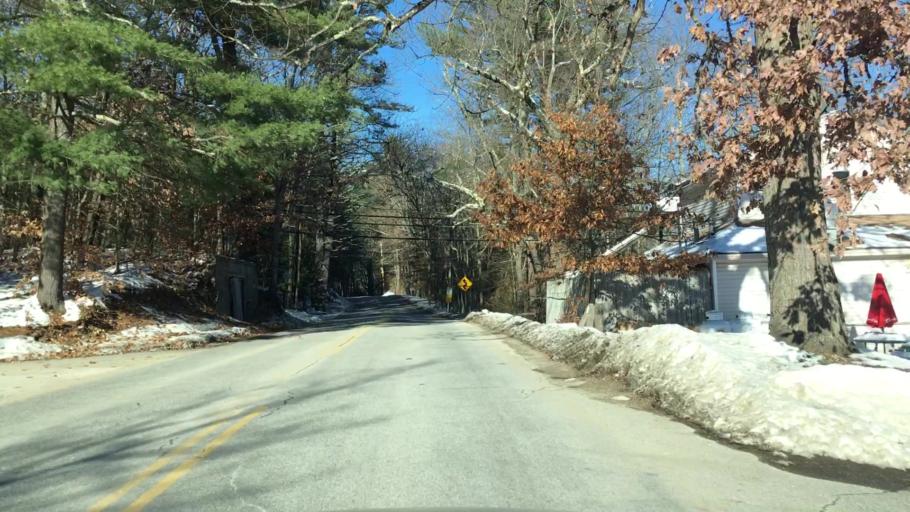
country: US
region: New Hampshire
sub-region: Hillsborough County
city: Mont Vernon
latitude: 42.8968
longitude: -71.6045
